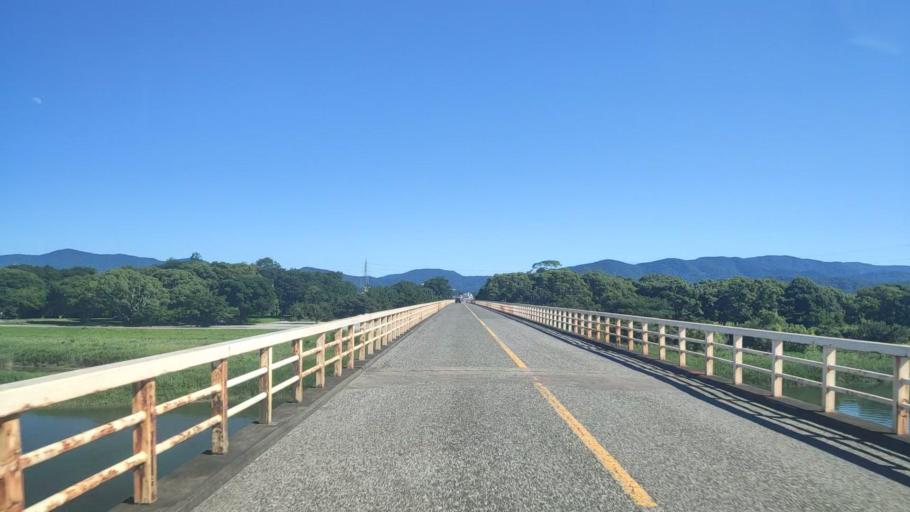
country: JP
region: Mie
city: Ise
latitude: 34.5109
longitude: 136.6928
